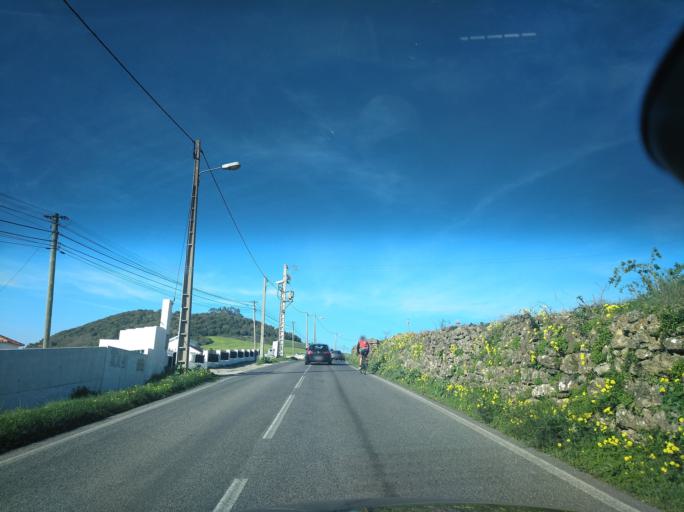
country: PT
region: Lisbon
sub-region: Sintra
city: Pero Pinheiro
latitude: 38.8945
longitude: -9.3269
